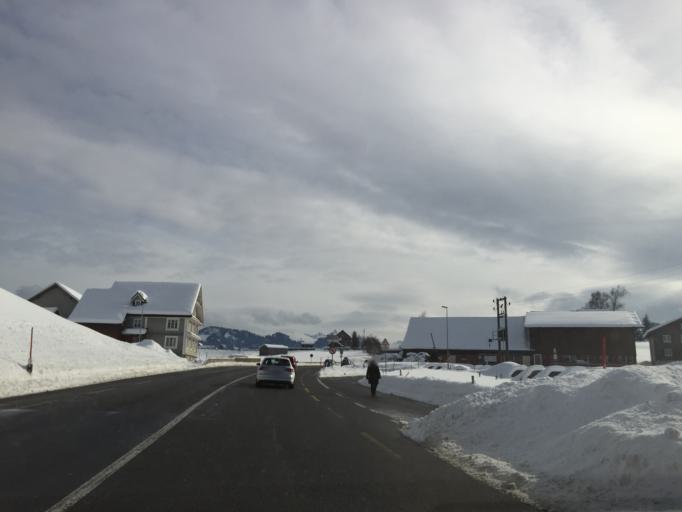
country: CH
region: Schwyz
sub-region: Bezirk Einsiedeln
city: Einsiedeln
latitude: 47.1418
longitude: 8.7540
